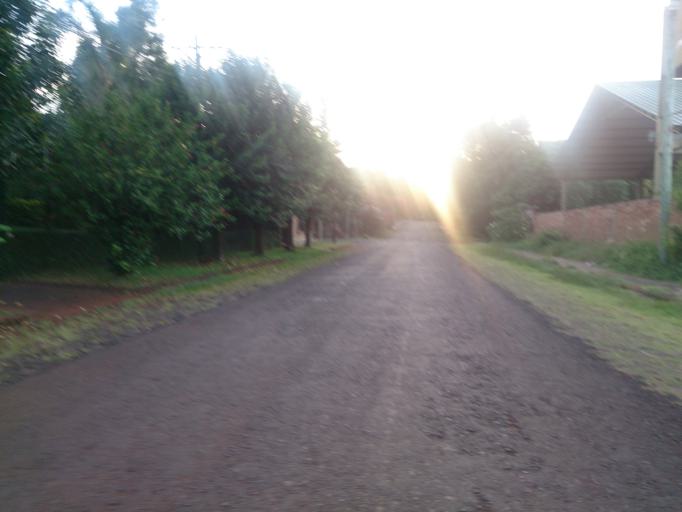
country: AR
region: Misiones
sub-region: Departamento de Obera
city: Obera
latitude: -27.4950
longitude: -55.1182
